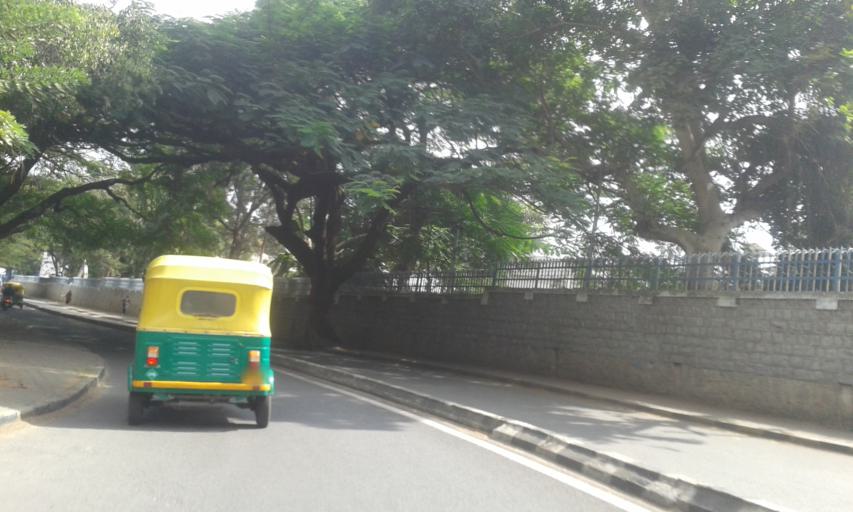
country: IN
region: Karnataka
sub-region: Bangalore Urban
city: Bangalore
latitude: 12.9653
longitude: 77.6267
